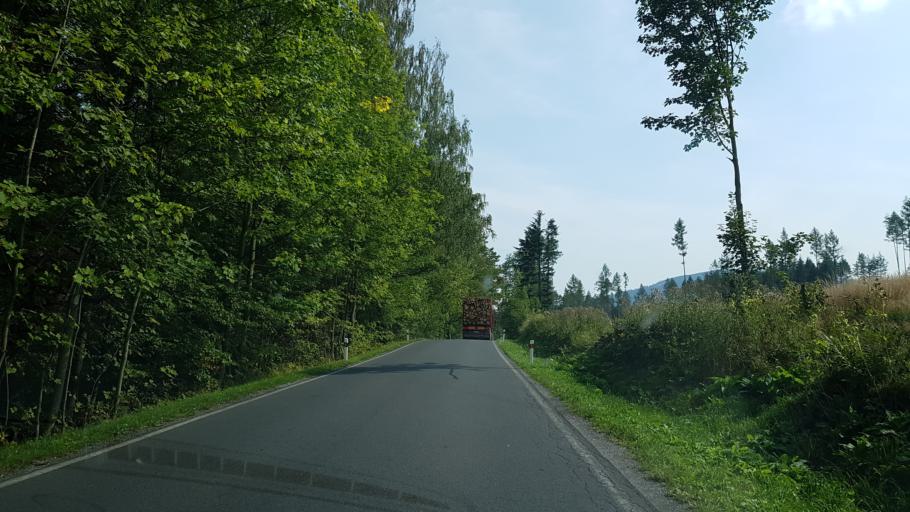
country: CZ
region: Olomoucky
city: Zlate Hory
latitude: 50.2488
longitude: 17.3636
